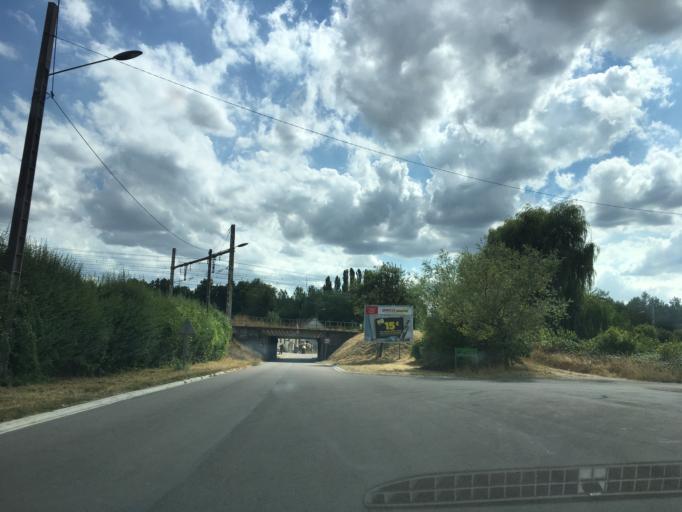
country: FR
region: Bourgogne
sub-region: Departement de l'Yonne
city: Joigny
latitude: 47.9733
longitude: 3.3846
